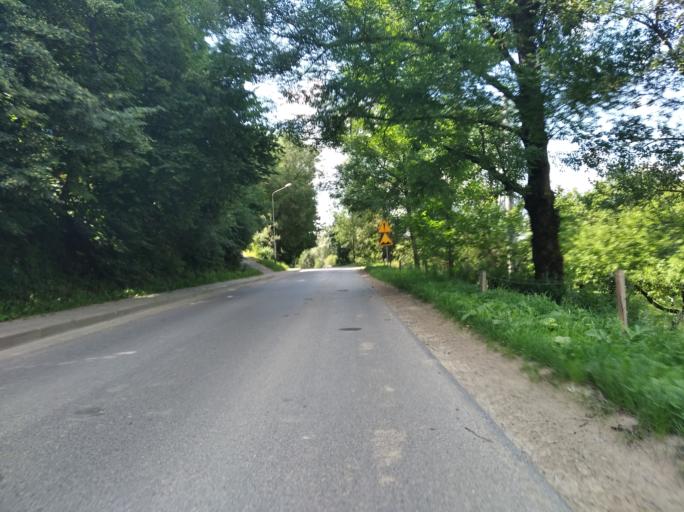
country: PL
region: Subcarpathian Voivodeship
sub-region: Powiat rzeszowski
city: Dynow
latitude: 49.8004
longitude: 22.2452
